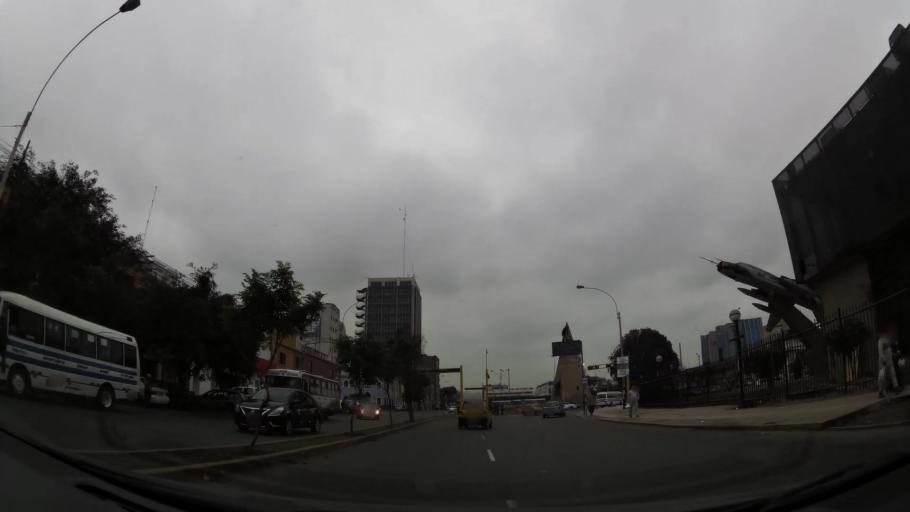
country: PE
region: Lima
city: Lima
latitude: -12.0644
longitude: -77.0403
